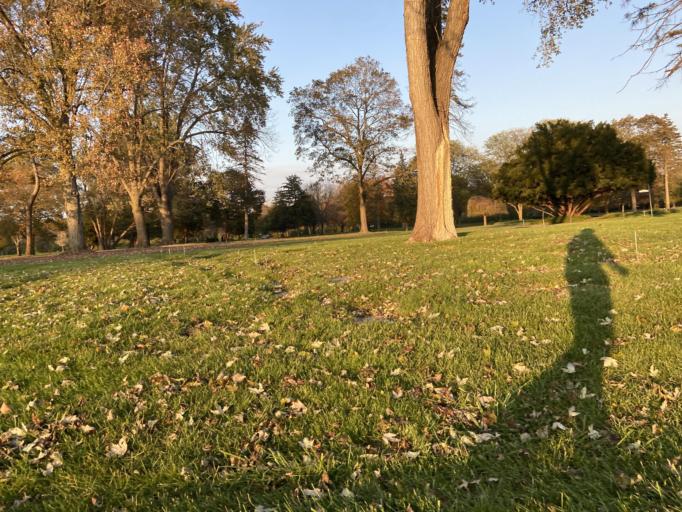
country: US
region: Michigan
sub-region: Wayne County
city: Redford
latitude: 42.4143
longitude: -83.3278
